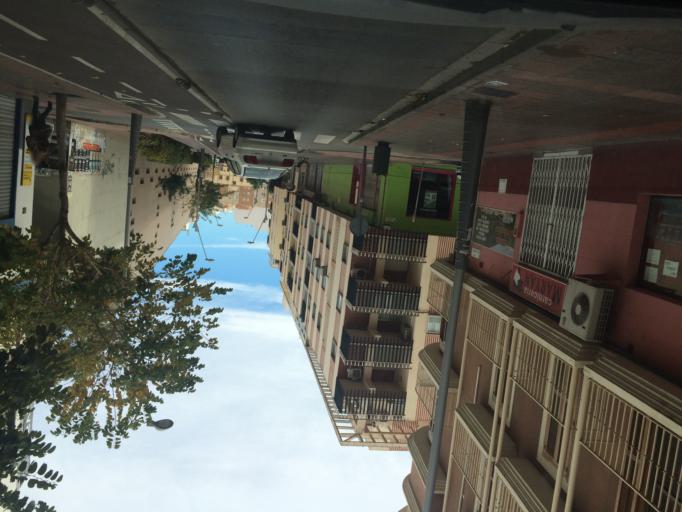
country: ES
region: Andalusia
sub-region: Provincia de Almeria
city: Almeria
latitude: 36.8425
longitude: -2.4556
